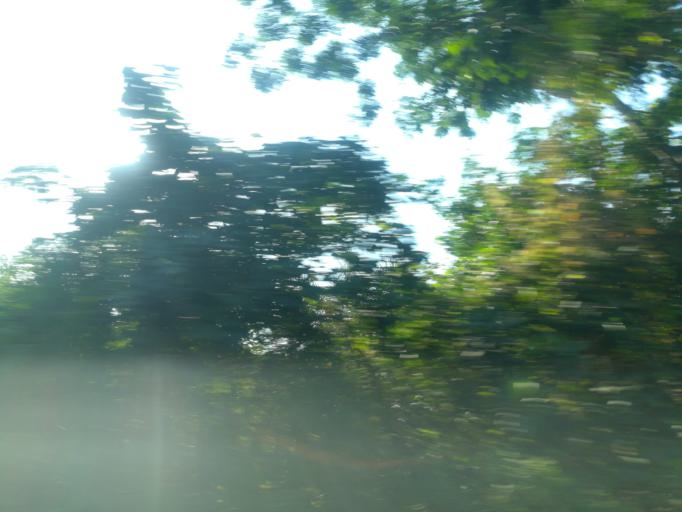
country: NG
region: Ogun
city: Abeokuta
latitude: 7.2483
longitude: 3.3005
